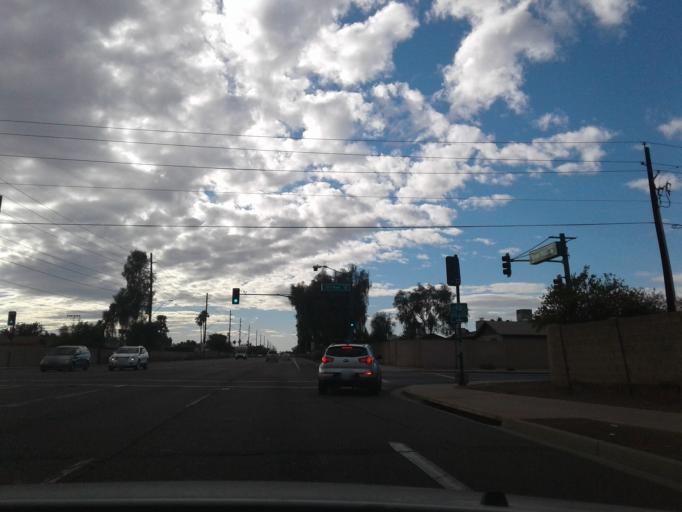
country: US
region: Arizona
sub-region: Maricopa County
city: Glendale
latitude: 33.6547
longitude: -112.0919
